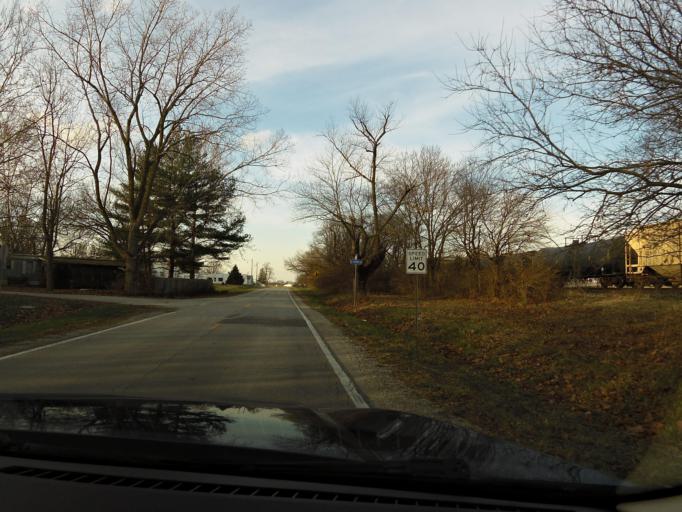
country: US
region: Illinois
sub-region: Fayette County
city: Vandalia
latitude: 38.9443
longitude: -89.1668
